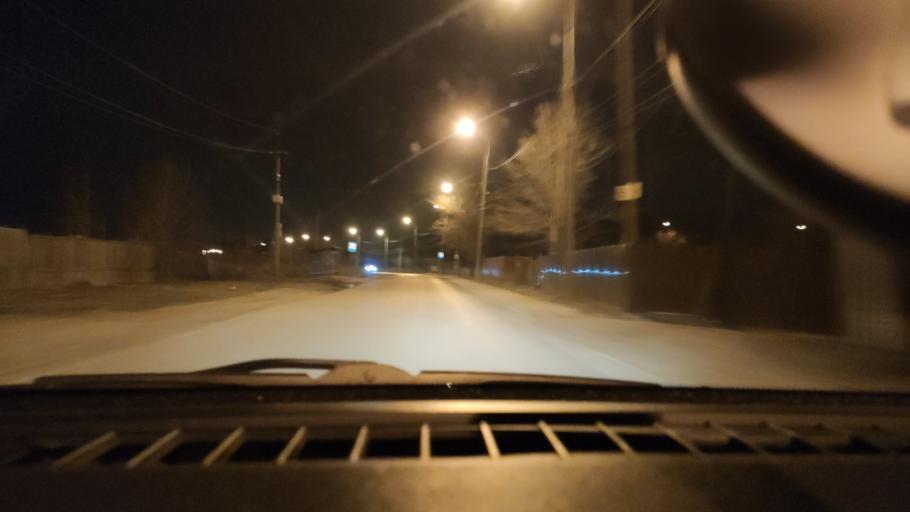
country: RU
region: Samara
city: Samara
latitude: 53.1413
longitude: 50.1314
